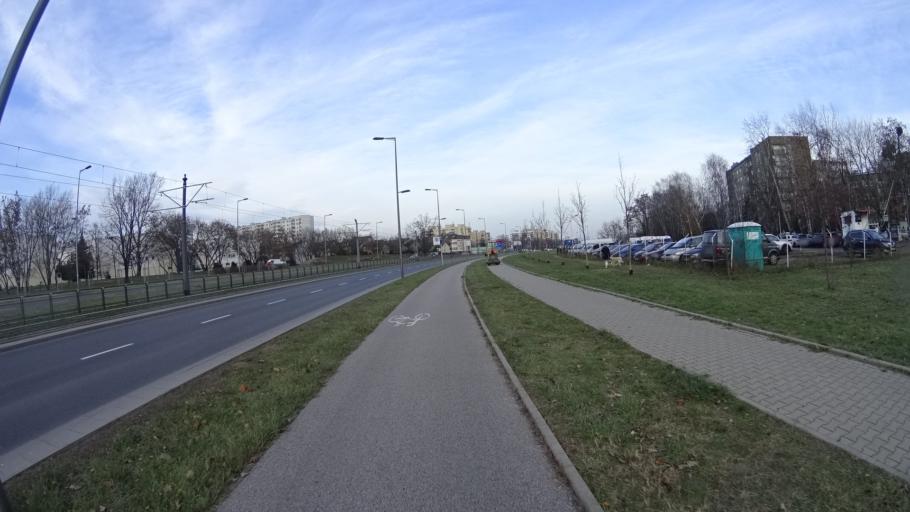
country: PL
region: Masovian Voivodeship
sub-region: Warszawa
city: Bemowo
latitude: 52.2496
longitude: 20.9113
